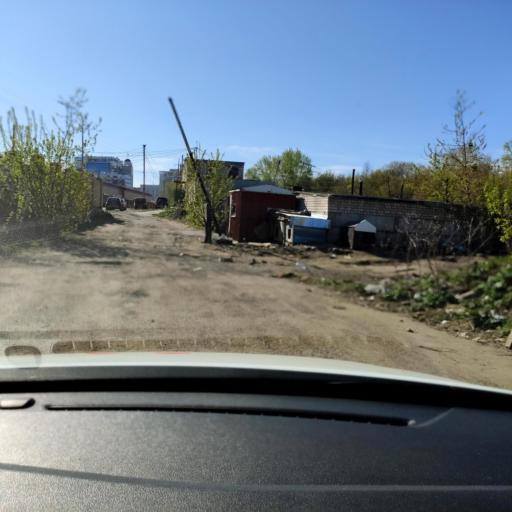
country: RU
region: Tatarstan
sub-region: Gorod Kazan'
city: Kazan
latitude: 55.7973
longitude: 49.1638
